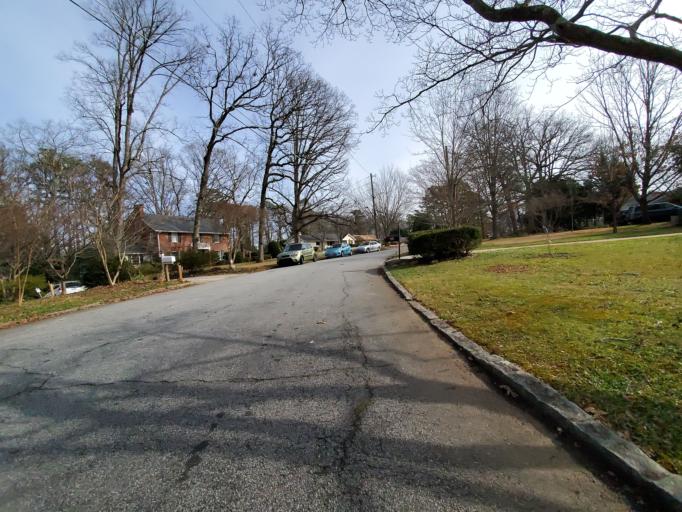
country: US
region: Georgia
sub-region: DeKalb County
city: North Decatur
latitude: 33.7771
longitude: -84.3182
